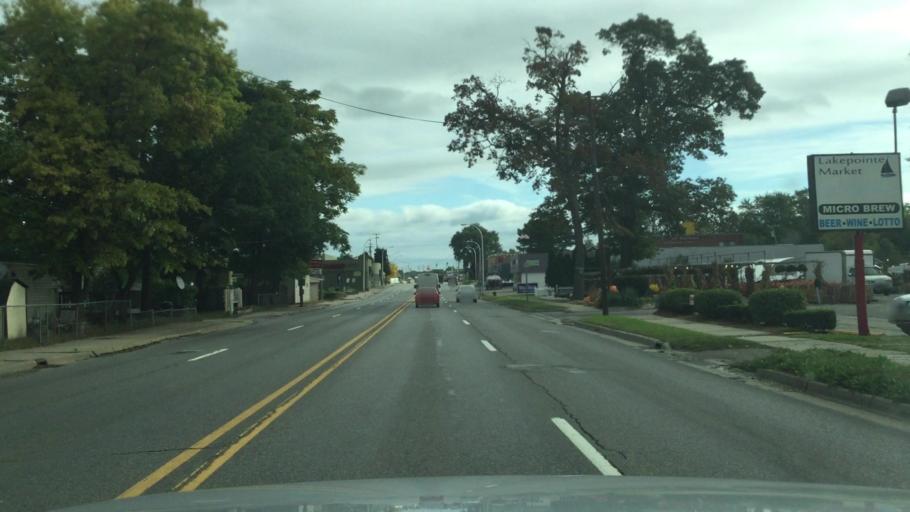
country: US
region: Michigan
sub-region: Oakland County
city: Keego Harbor
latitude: 42.6043
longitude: -83.3477
